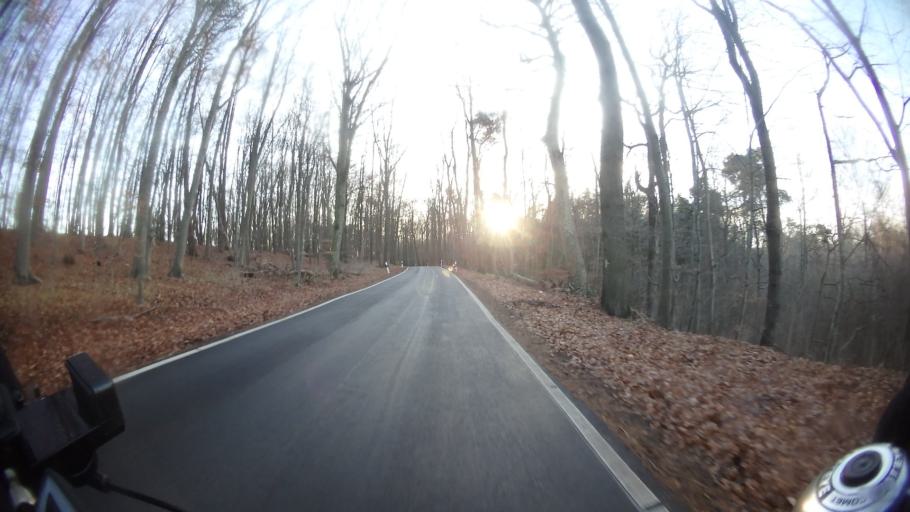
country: DE
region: Schleswig-Holstein
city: Ratekau
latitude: 53.9134
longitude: 10.7847
